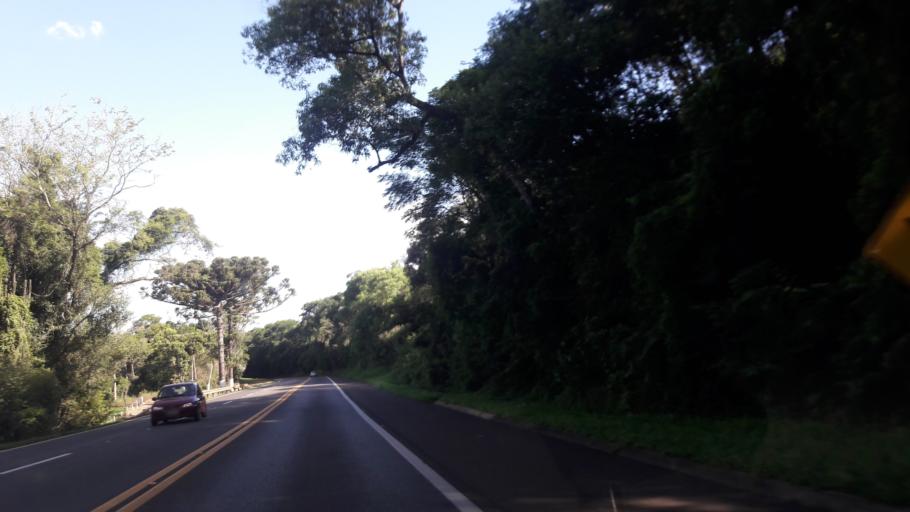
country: BR
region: Parana
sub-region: Laranjeiras Do Sul
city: Laranjeiras do Sul
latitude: -25.4071
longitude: -52.0901
